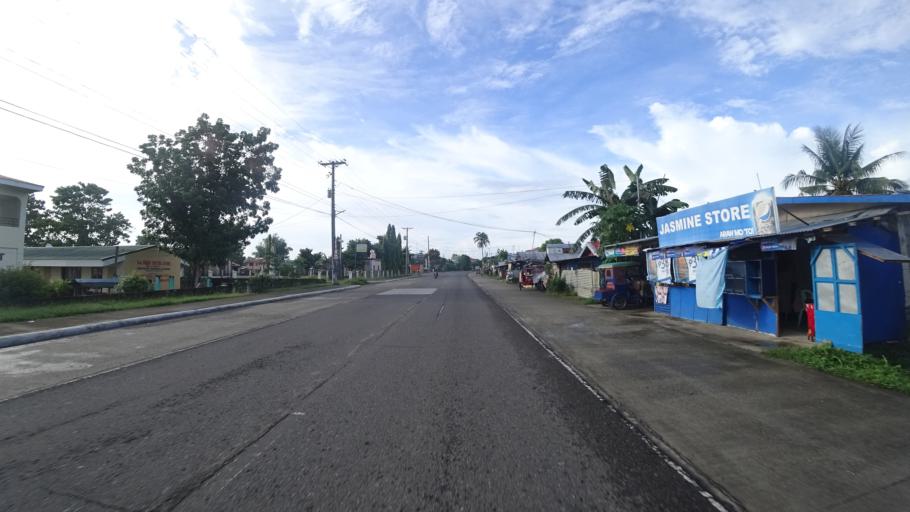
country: PH
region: Eastern Visayas
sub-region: Province of Leyte
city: Palo
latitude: 11.1417
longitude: 125.0045
